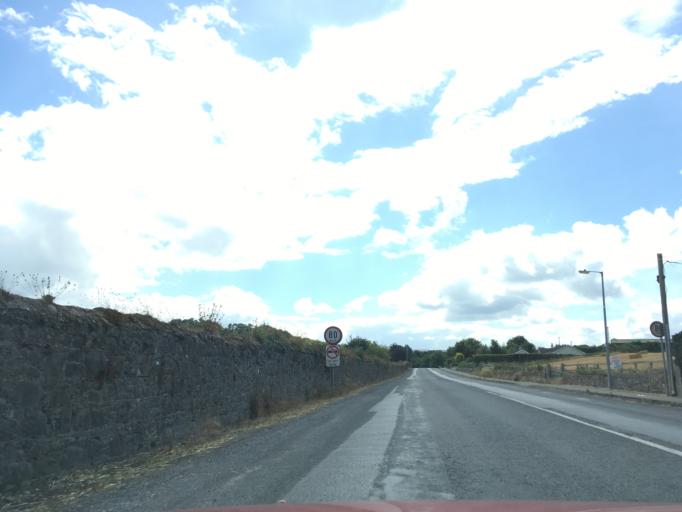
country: IE
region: Munster
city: Cahir
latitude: 52.3697
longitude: -7.9318
